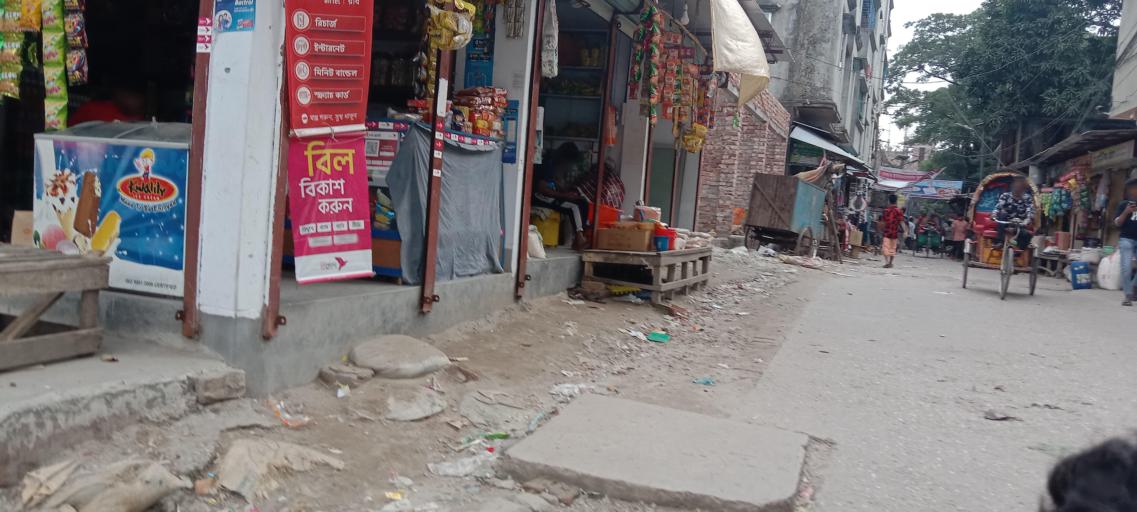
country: BD
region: Dhaka
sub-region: Dhaka
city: Dhaka
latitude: 23.6986
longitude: 90.4093
